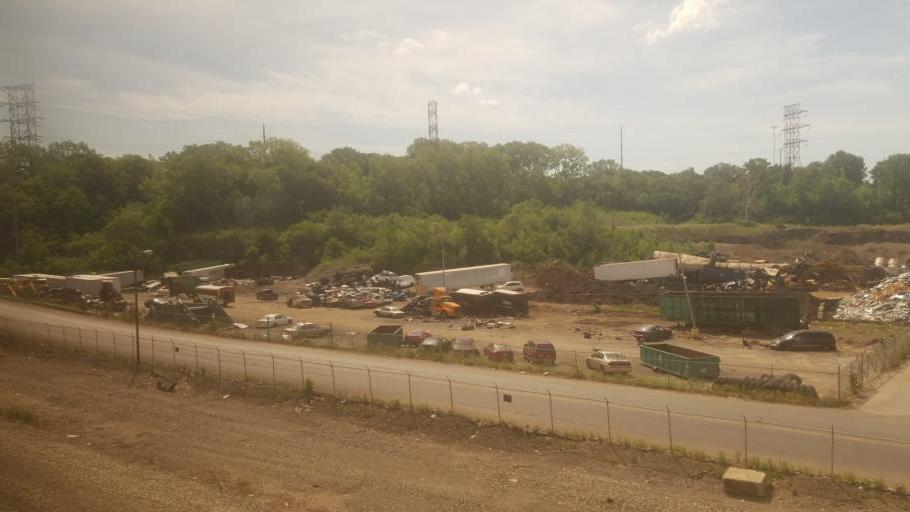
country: US
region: Missouri
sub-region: Jackson County
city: Sugar Creek
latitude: 39.1120
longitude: -94.4908
